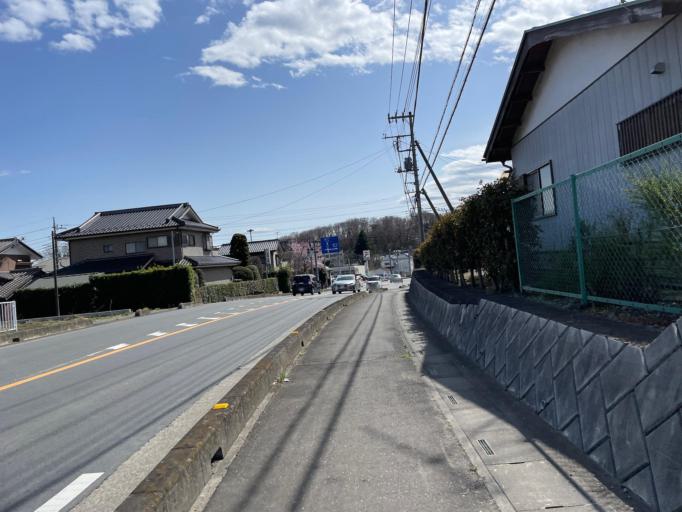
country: JP
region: Saitama
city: Morohongo
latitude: 35.9871
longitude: 139.3322
